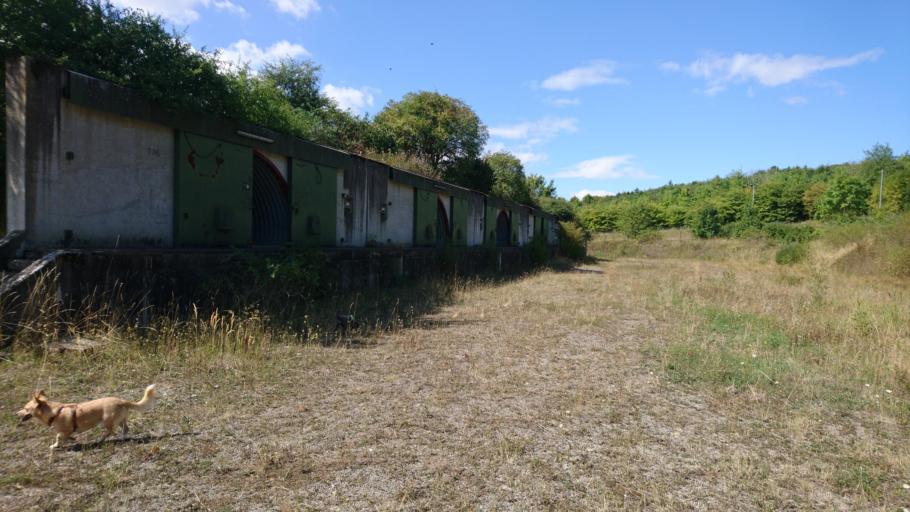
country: DE
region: Bavaria
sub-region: Regierungsbezirk Unterfranken
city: Rannungen
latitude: 50.1397
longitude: 10.2337
